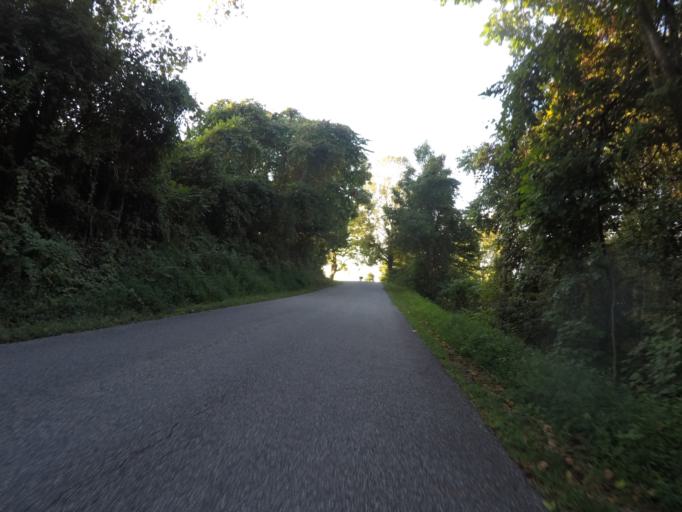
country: US
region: Ohio
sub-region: Lawrence County
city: Coal Grove
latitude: 38.5966
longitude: -82.5466
